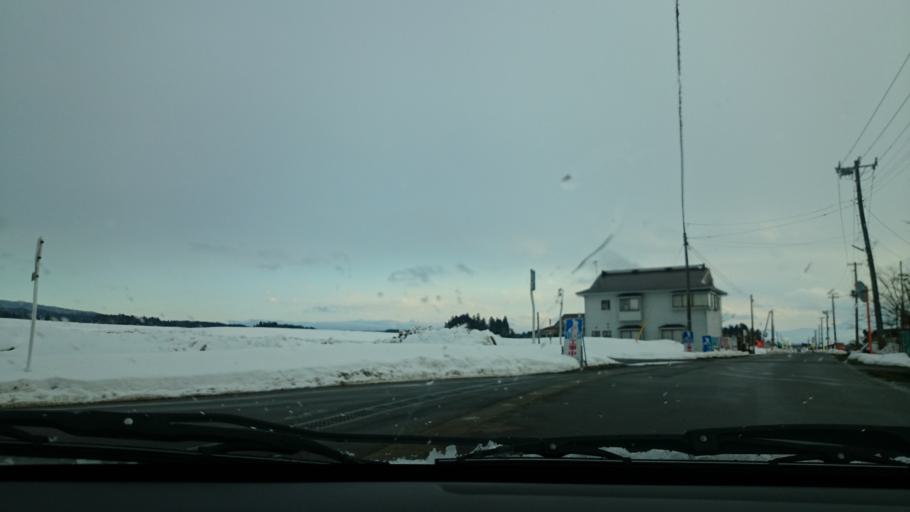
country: JP
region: Fukushima
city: Kitakata
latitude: 37.6311
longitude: 139.9220
